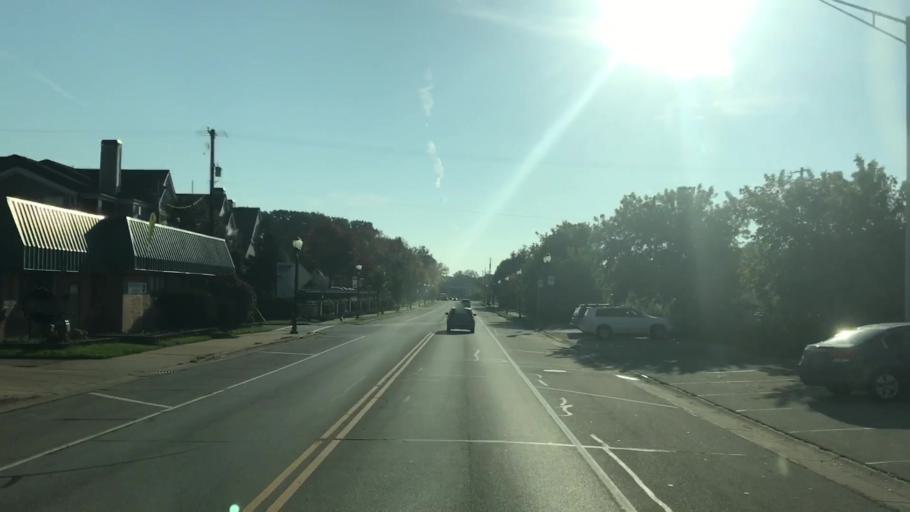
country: US
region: Wisconsin
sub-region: Milwaukee County
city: Wauwatosa
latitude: 43.0445
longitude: -87.9907
